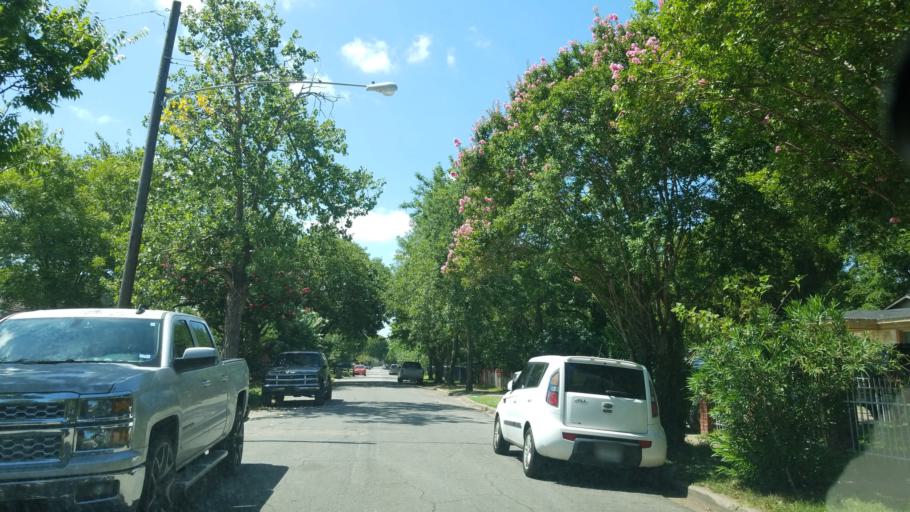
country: US
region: Texas
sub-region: Dallas County
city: Balch Springs
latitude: 32.7458
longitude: -96.6952
